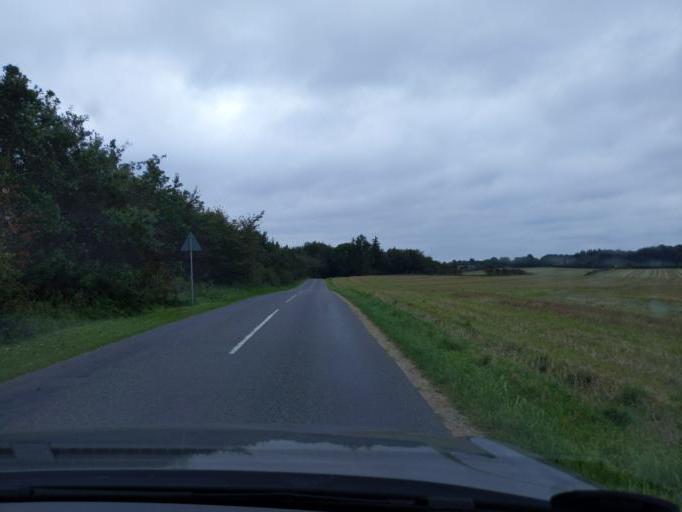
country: DK
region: North Denmark
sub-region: Mariagerfjord Kommune
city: Hobro
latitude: 56.5508
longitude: 9.6498
